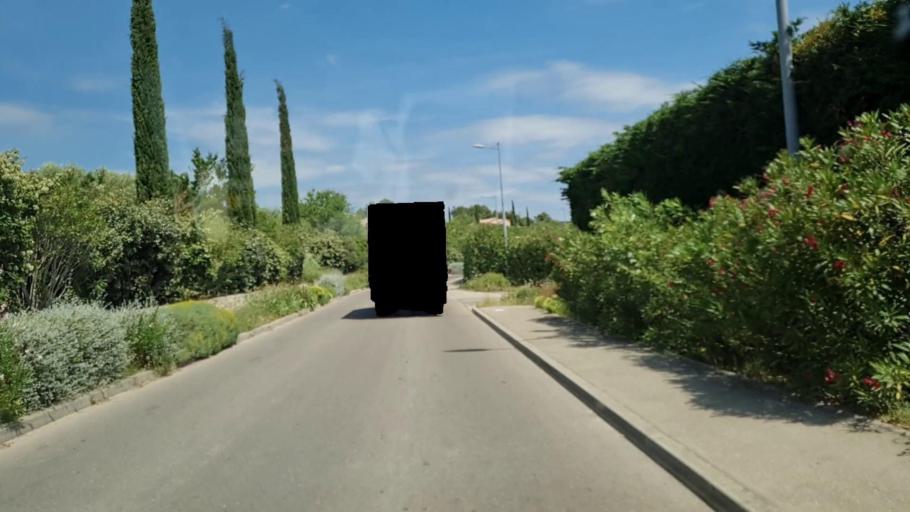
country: FR
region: Languedoc-Roussillon
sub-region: Departement du Gard
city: Cabrieres
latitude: 43.8986
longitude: 4.4730
